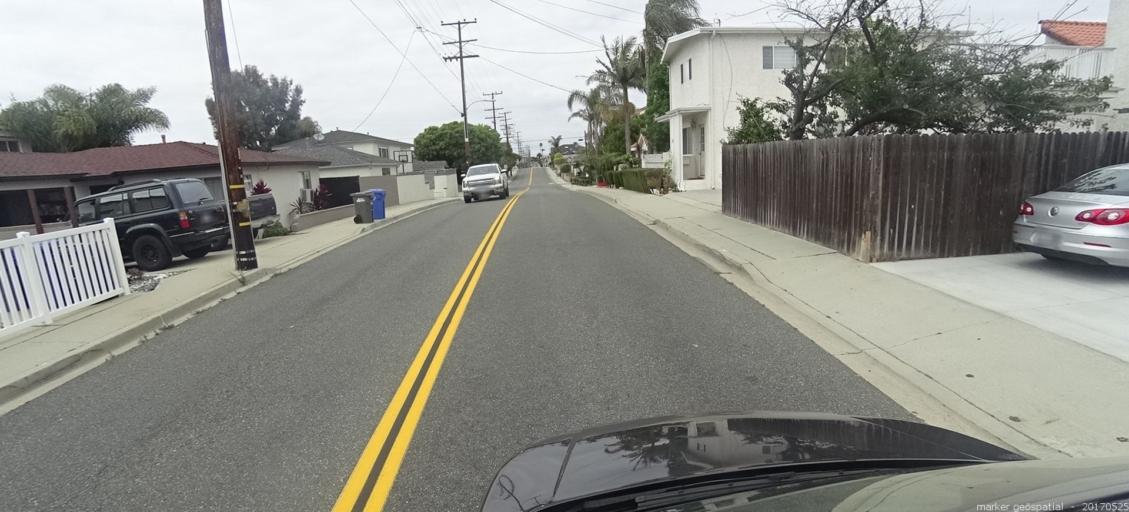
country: US
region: California
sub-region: Los Angeles County
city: Redondo Beach
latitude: 33.8654
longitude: -118.3791
